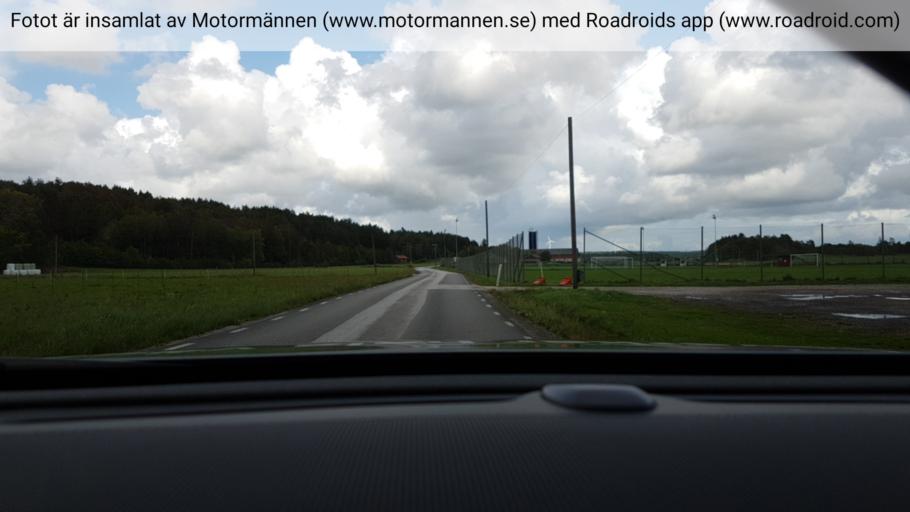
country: SE
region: Vaestra Goetaland
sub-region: Orust
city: Henan
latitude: 58.1421
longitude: 11.5703
